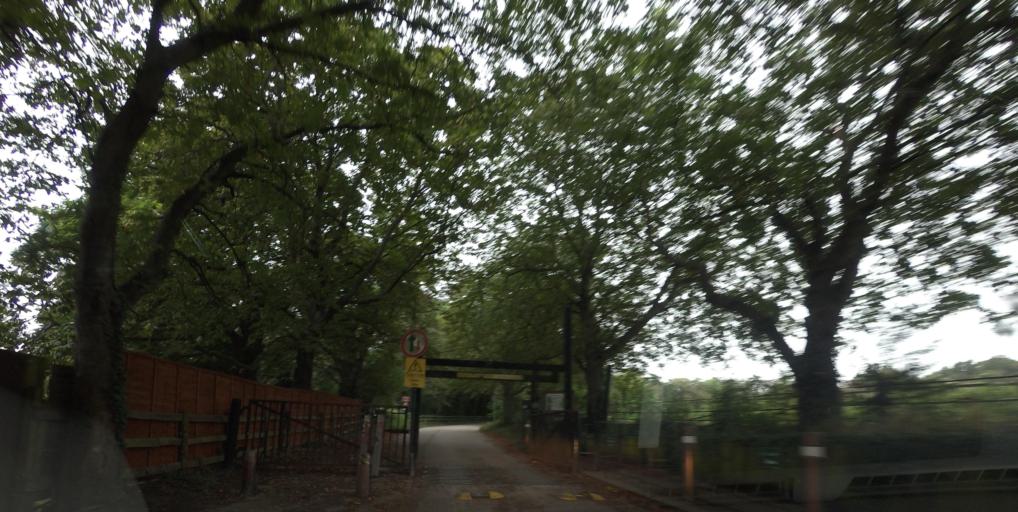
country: GB
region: England
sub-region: Kent
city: Stone
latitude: 51.4289
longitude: 0.2485
